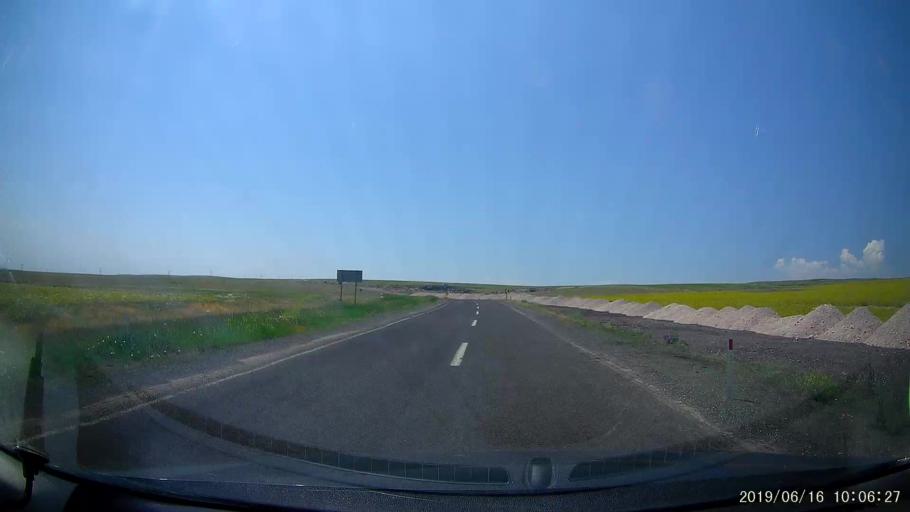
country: TR
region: Kars
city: Digor
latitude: 40.2551
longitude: 43.5426
